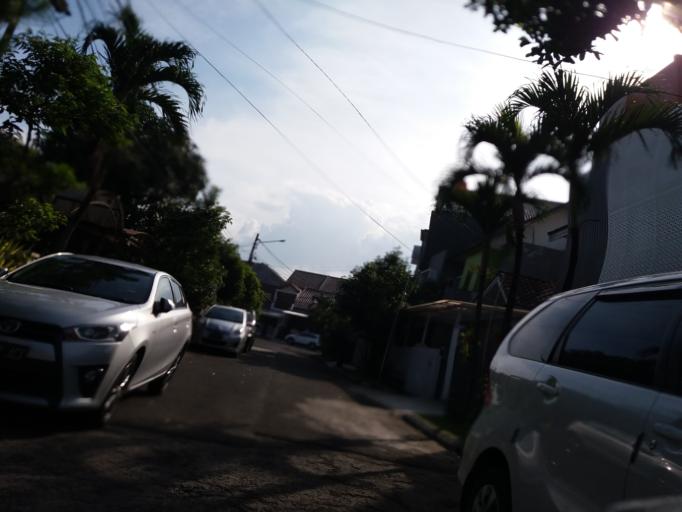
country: ID
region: West Java
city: Bandung
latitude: -6.9628
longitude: 107.6307
